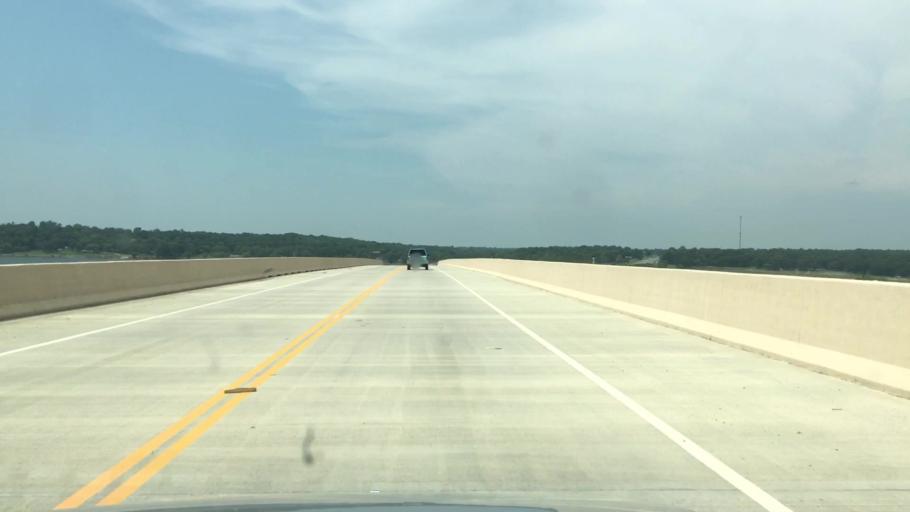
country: US
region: Oklahoma
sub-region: Wagoner County
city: Wagoner
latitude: 35.9299
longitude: -95.2677
